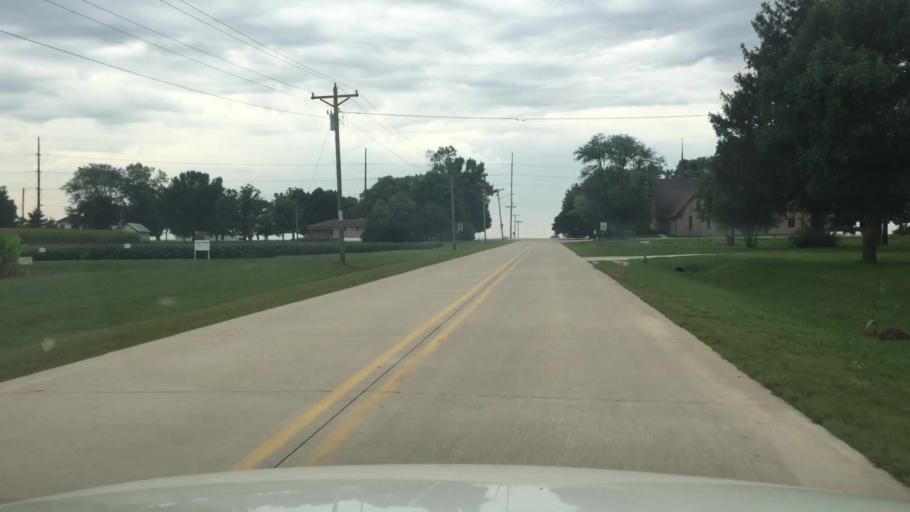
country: US
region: Iowa
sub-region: Story County
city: Huxley
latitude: 41.8799
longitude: -93.5809
